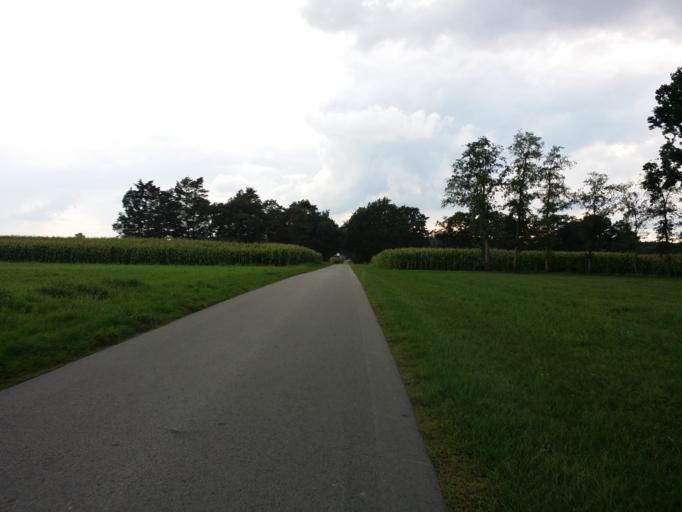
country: DE
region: Lower Saxony
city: Hemmoor
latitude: 53.6684
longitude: 9.1443
